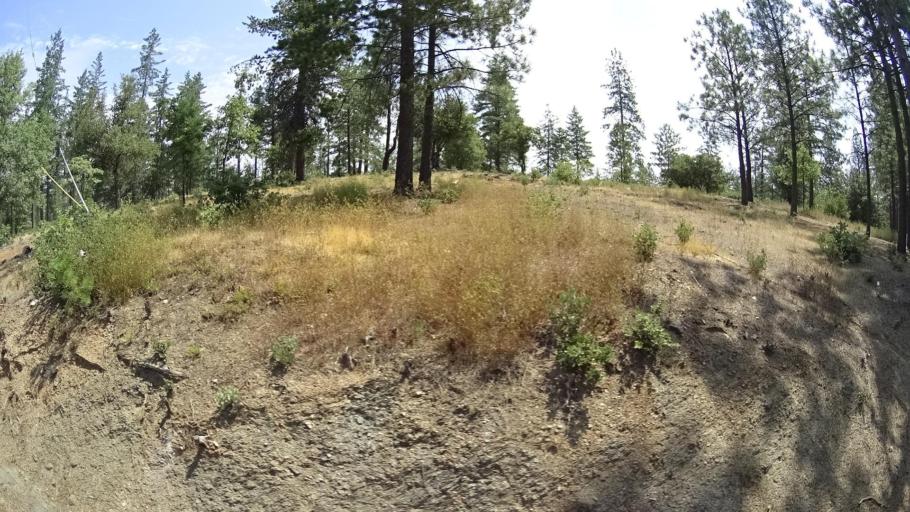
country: US
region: California
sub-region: Tuolumne County
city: Tuolumne City
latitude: 37.7315
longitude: -120.1227
